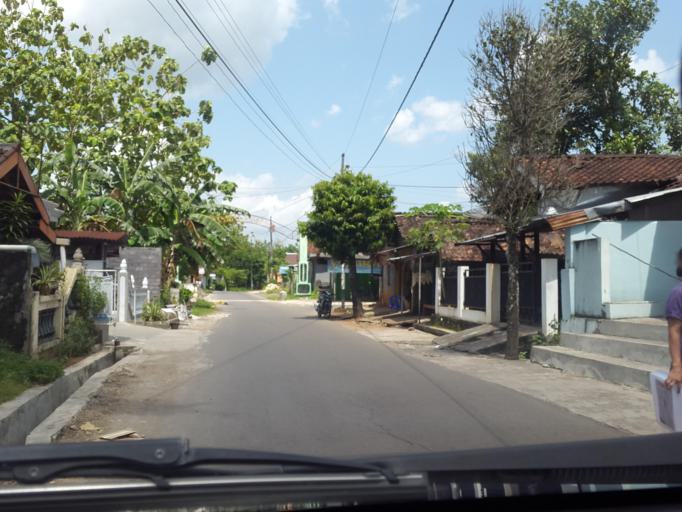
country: ID
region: Central Java
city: Selogiri
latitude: -7.8665
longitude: 110.7373
